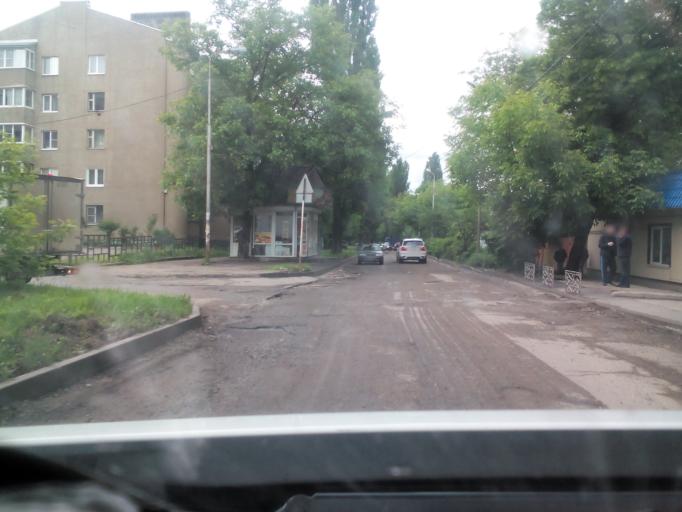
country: RU
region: Stavropol'skiy
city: Pyatigorsk
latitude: 44.0508
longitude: 43.0581
